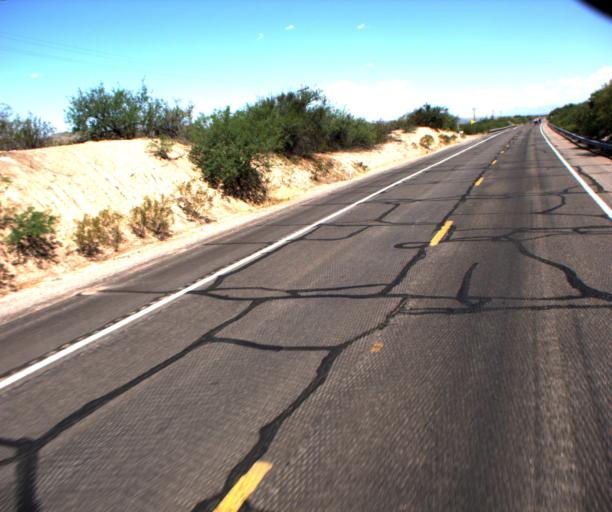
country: US
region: Arizona
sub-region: Pinal County
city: Mammoth
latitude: 32.7948
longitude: -110.6754
